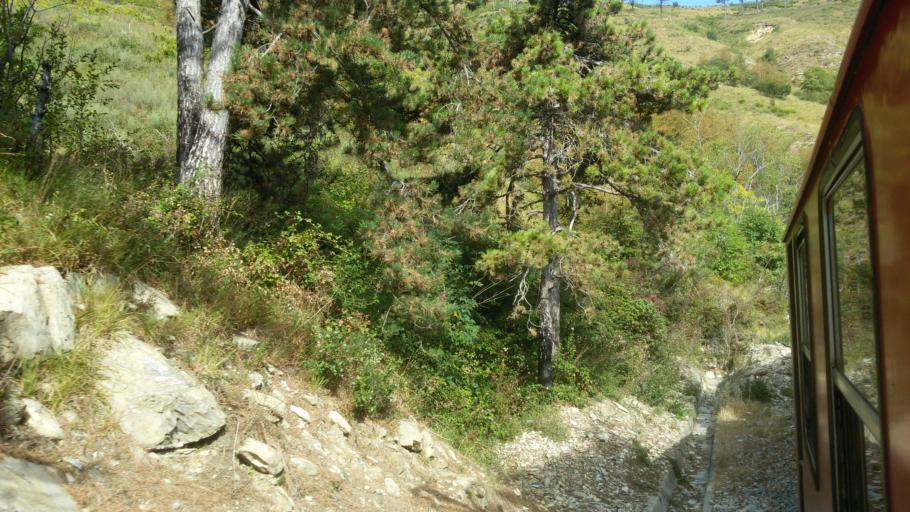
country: IT
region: Liguria
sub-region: Provincia di Genova
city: Manesseno
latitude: 44.4472
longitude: 8.9437
